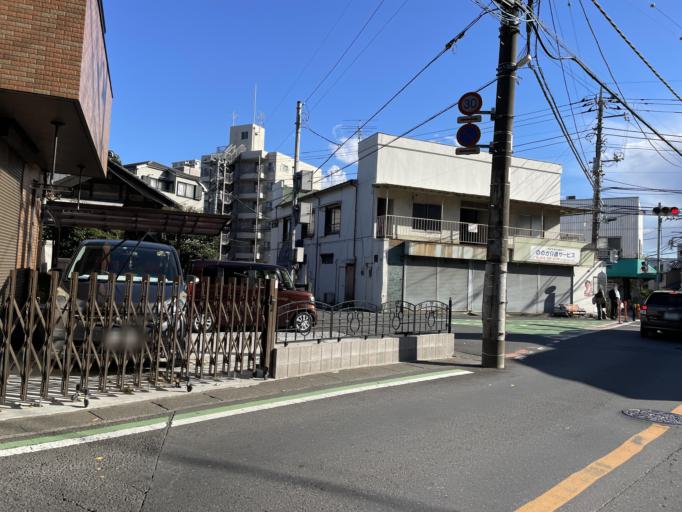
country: JP
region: Saitama
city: Wako
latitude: 35.7915
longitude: 139.6351
